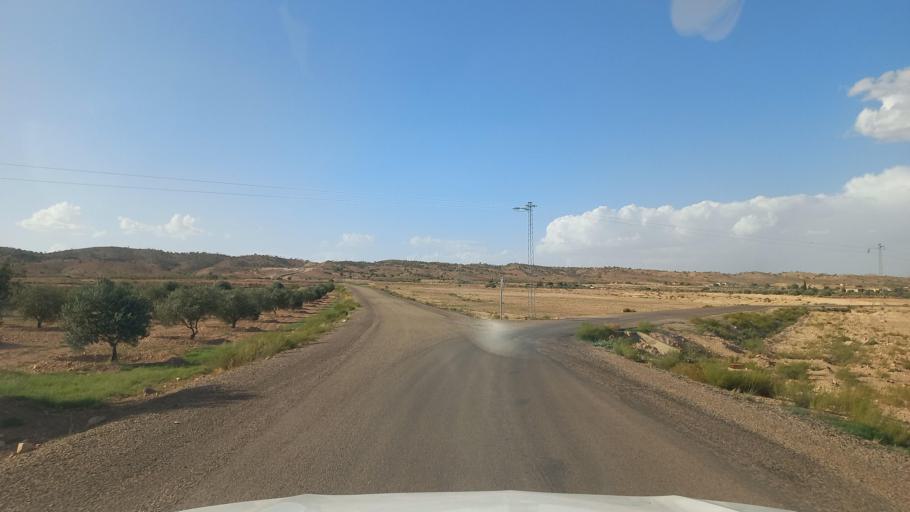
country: TN
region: Al Qasrayn
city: Sbiba
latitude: 35.3485
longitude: 8.9888
